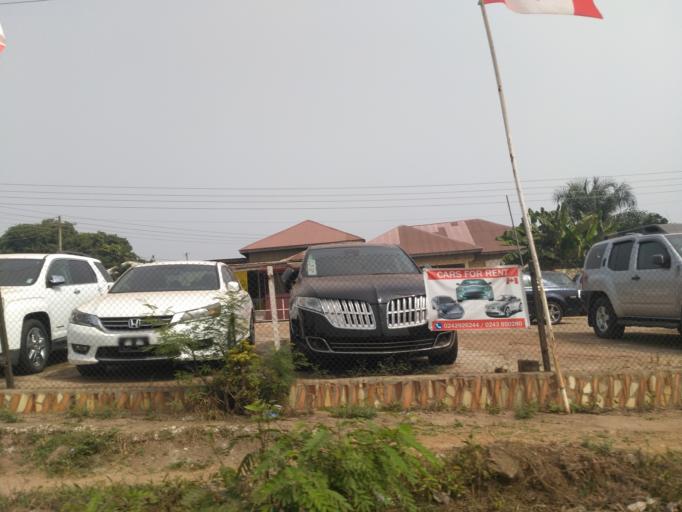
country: GH
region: Ashanti
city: Kumasi
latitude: 6.6706
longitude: -1.6355
